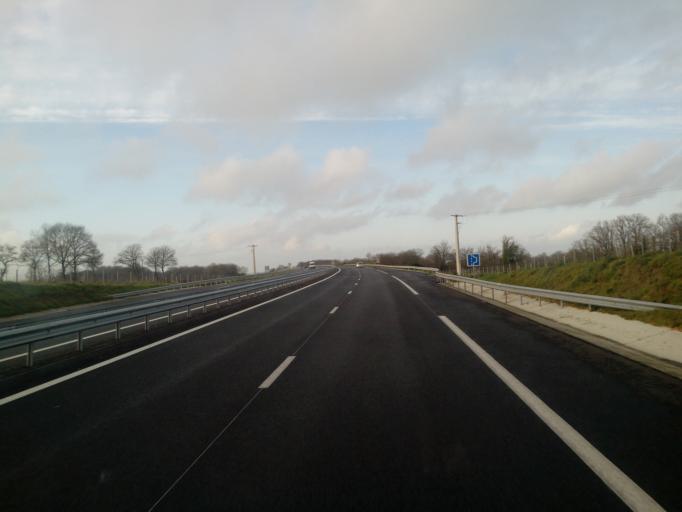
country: FR
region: Poitou-Charentes
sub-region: Departement des Deux-Sevres
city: Nueil-les-Aubiers
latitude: 46.8702
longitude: -0.5775
